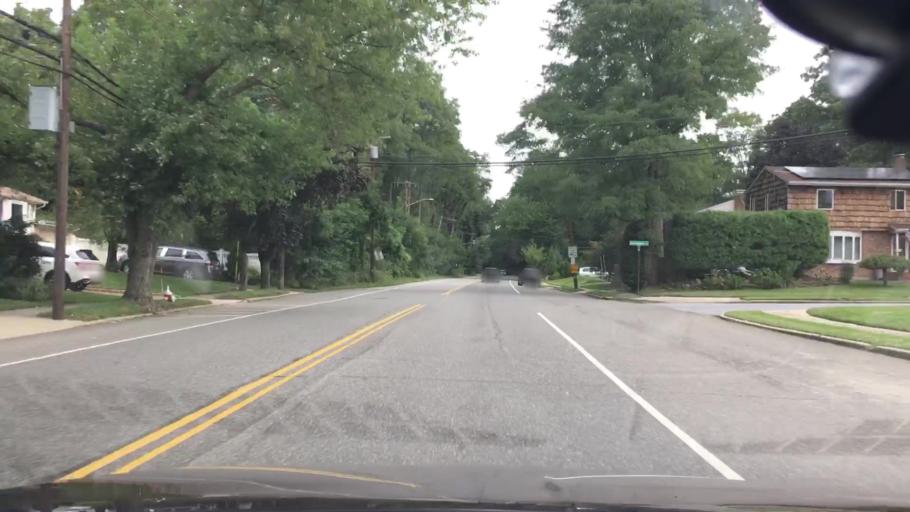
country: US
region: New York
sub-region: Nassau County
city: Old Bethpage
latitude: 40.7710
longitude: -73.4504
